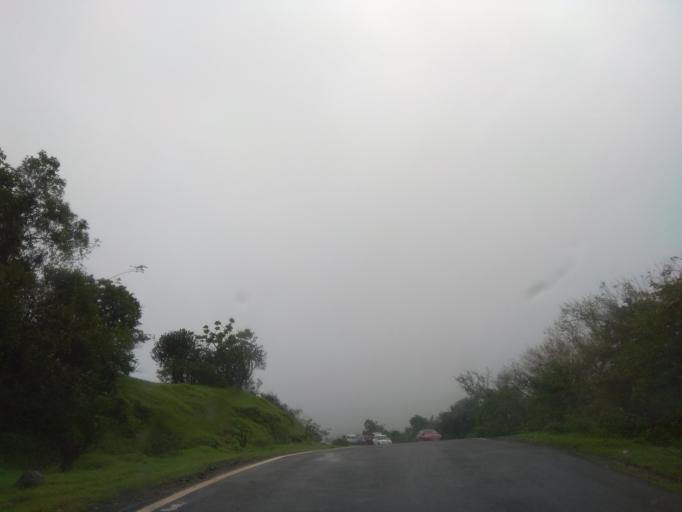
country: IN
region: Maharashtra
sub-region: Raigarh
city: Indapur
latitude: 18.4921
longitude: 73.4236
